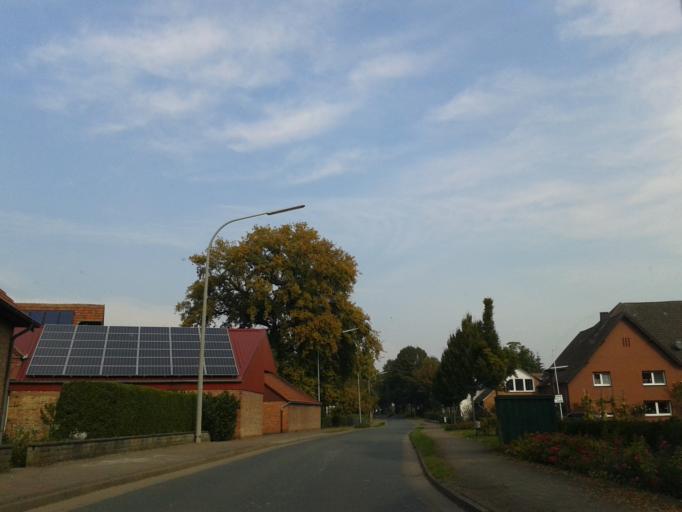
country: DE
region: North Rhine-Westphalia
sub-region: Regierungsbezirk Detmold
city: Salzkotten
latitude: 51.7171
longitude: 8.6266
